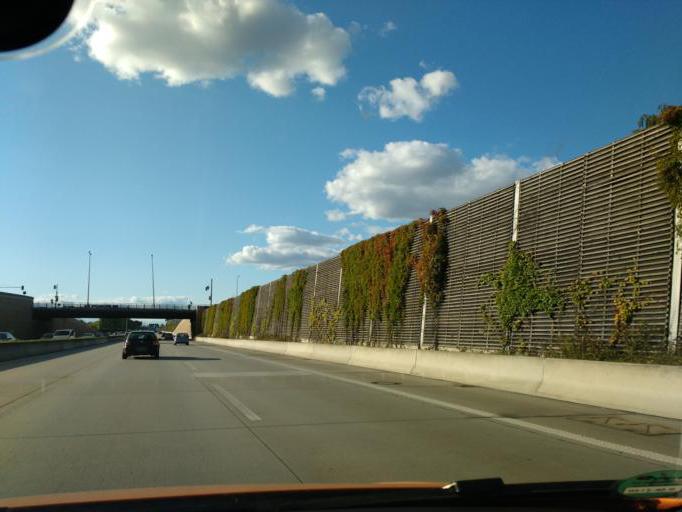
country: DE
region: Berlin
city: Rudow
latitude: 52.4424
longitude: 13.4805
